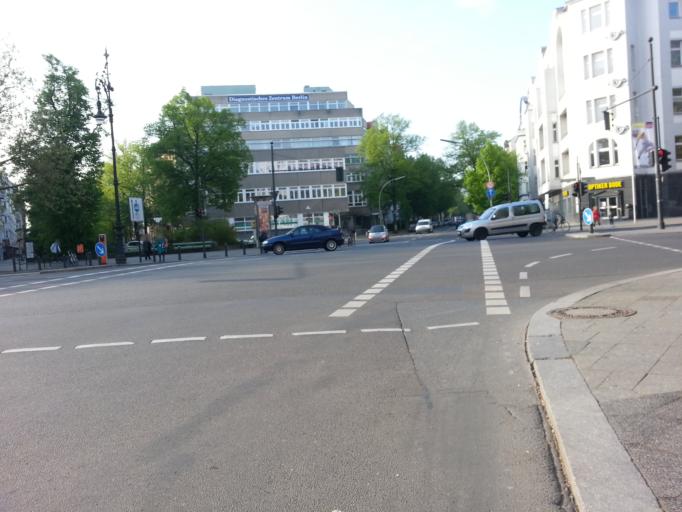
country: DE
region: Berlin
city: Halensee
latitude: 52.4982
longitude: 13.2959
